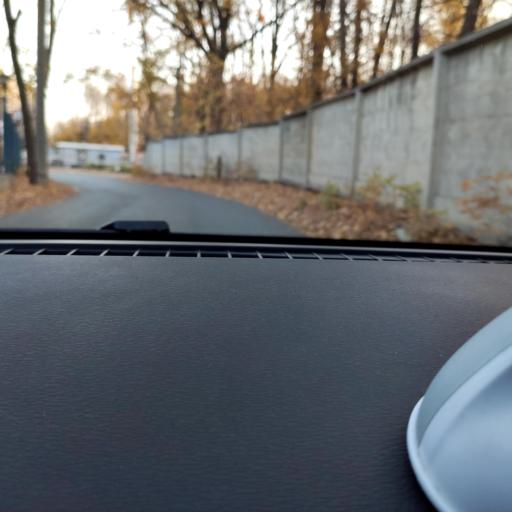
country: RU
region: Samara
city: Samara
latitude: 53.2625
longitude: 50.2450
